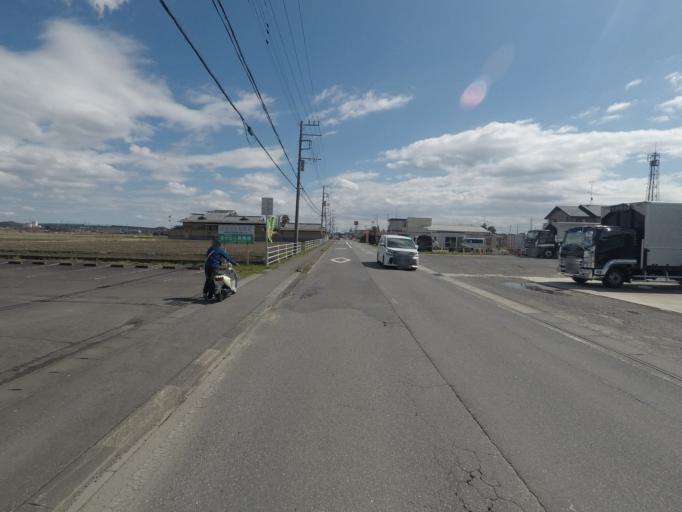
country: JP
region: Ibaraki
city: Fujishiro
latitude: 35.9356
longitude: 140.1244
